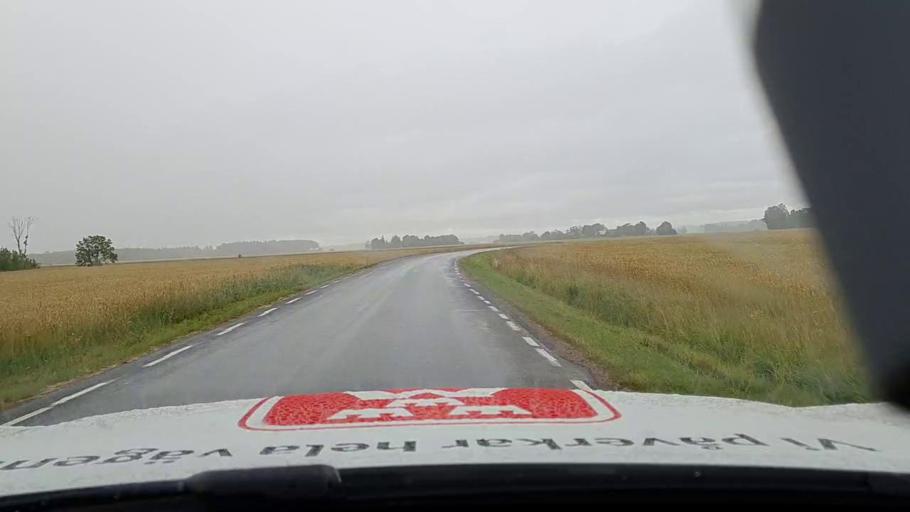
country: SE
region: Vaestra Goetaland
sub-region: Toreboda Kommun
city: Toereboda
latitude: 58.6532
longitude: 14.1070
